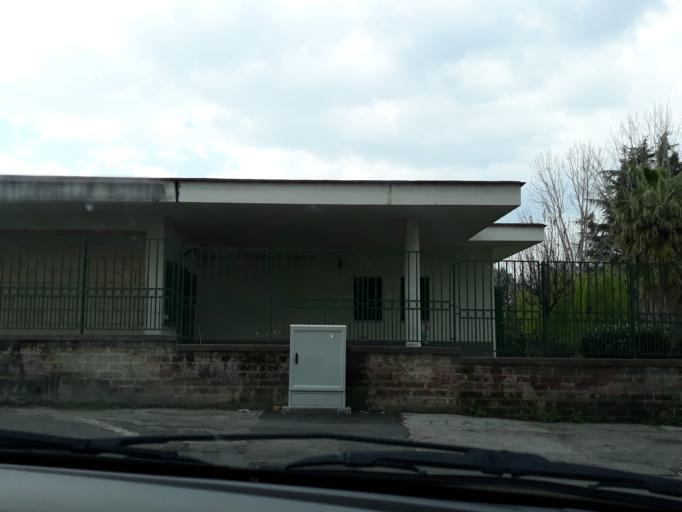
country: IT
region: Campania
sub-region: Provincia di Napoli
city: Melito di Napoli
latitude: 40.8919
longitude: 14.2317
